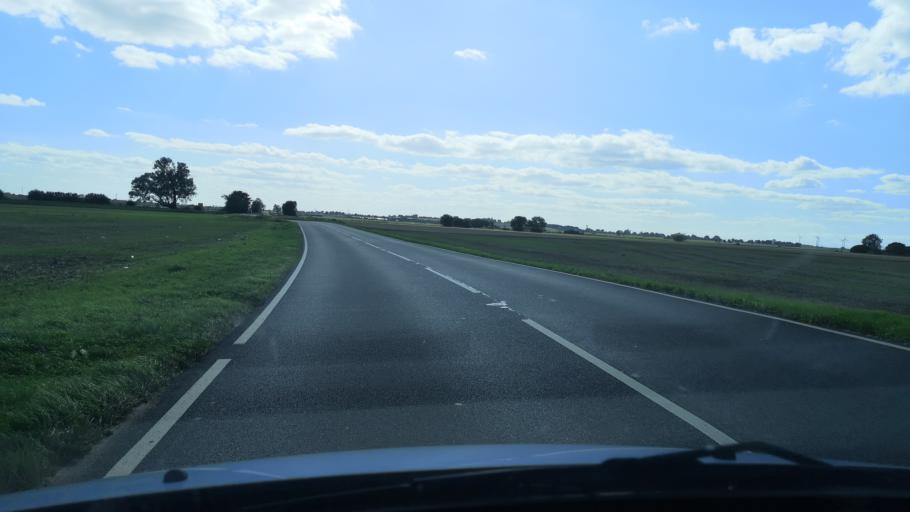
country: GB
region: England
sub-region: North Lincolnshire
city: Eastoft
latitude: 53.6264
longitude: -0.8013
